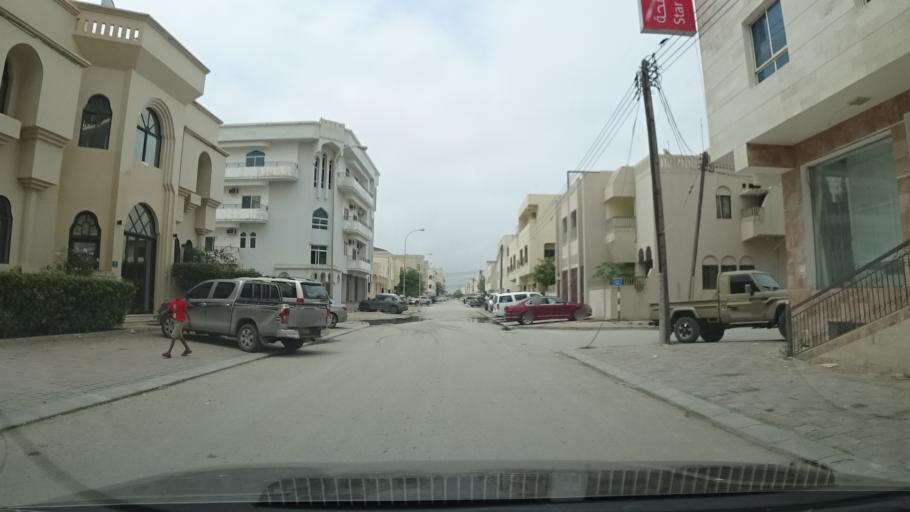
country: OM
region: Zufar
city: Salalah
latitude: 17.0180
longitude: 54.0865
